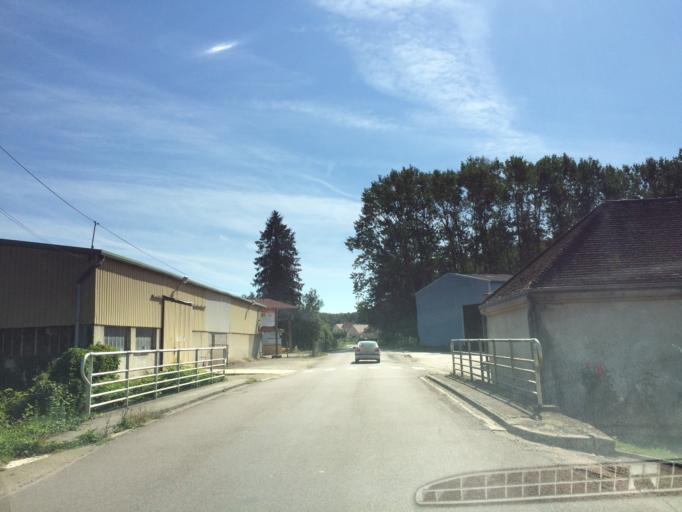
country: FR
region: Bourgogne
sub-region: Departement de l'Yonne
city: Aillant-sur-Tholon
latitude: 47.8340
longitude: 3.3642
